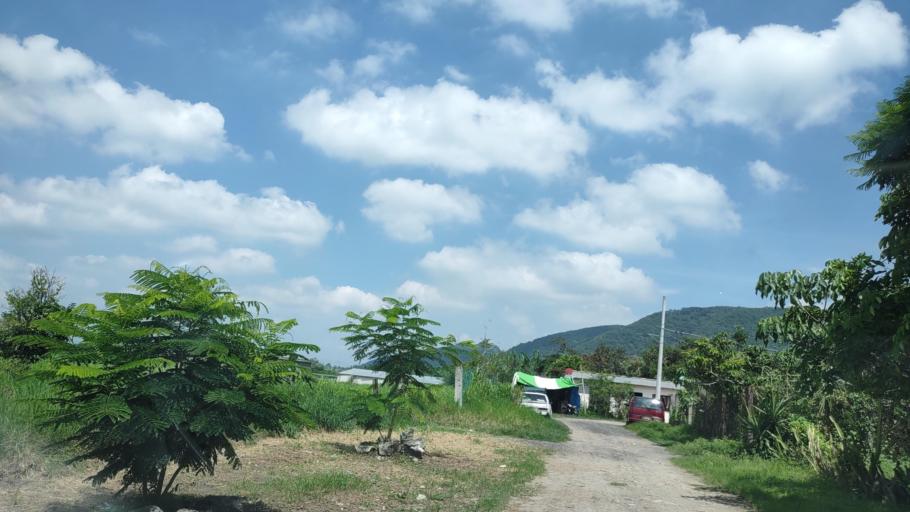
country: MX
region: Veracruz
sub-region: Emiliano Zapata
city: Dos Rios
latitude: 19.4301
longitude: -96.8084
